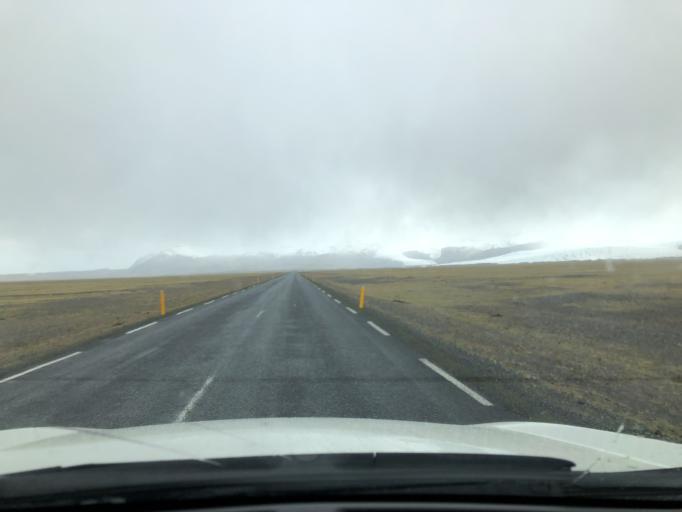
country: IS
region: East
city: Hoefn
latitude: 64.0291
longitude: -16.3118
